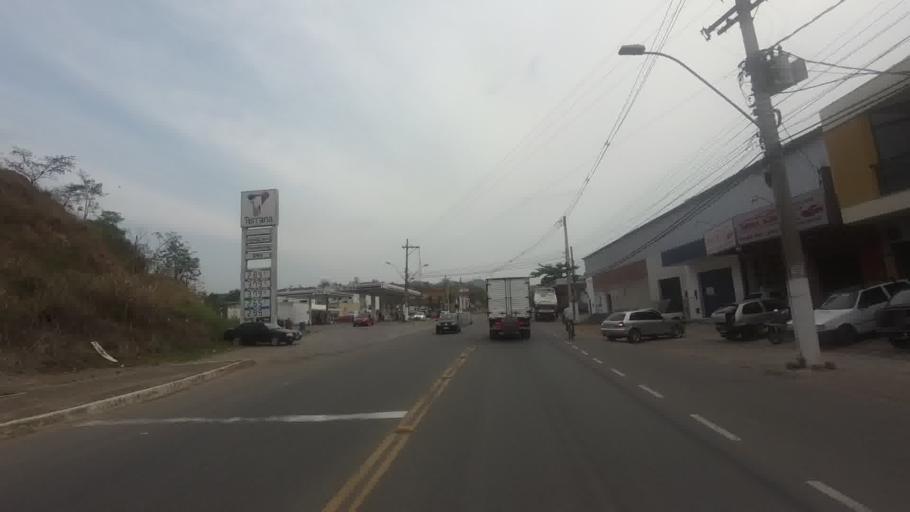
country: BR
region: Rio de Janeiro
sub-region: Santo Antonio De Padua
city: Santo Antonio de Padua
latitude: -21.5524
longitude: -42.1783
